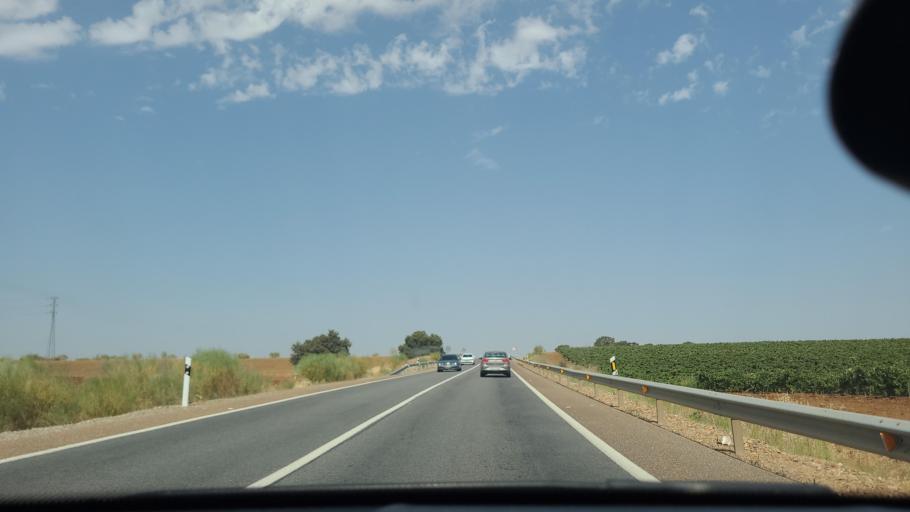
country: ES
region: Extremadura
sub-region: Provincia de Badajoz
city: Entrin Bajo
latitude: 38.6549
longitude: -6.7218
